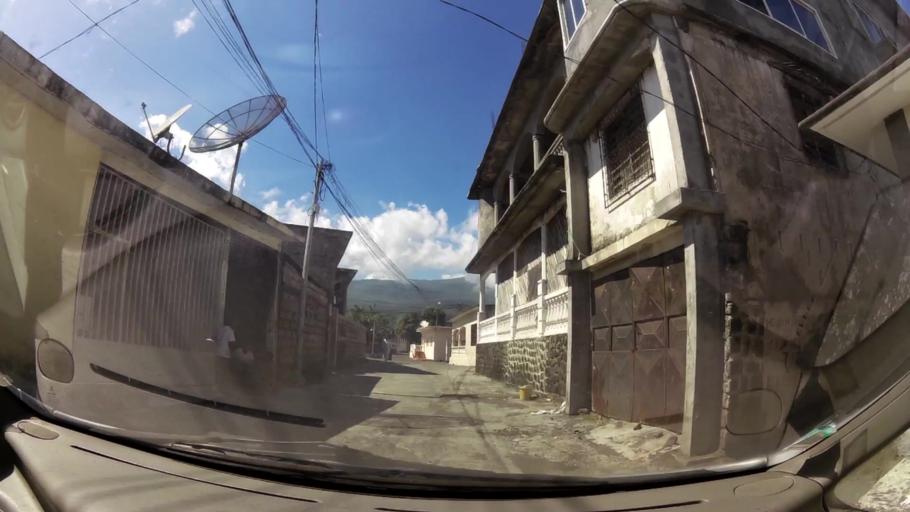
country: KM
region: Grande Comore
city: Mavingouni
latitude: -11.7474
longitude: 43.2348
